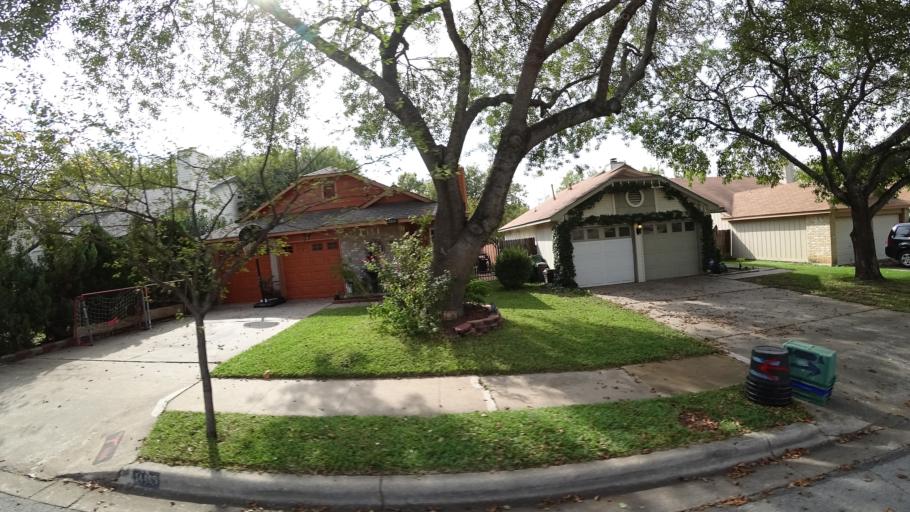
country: US
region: Texas
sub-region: Travis County
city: Wells Branch
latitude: 30.4404
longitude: -97.6858
